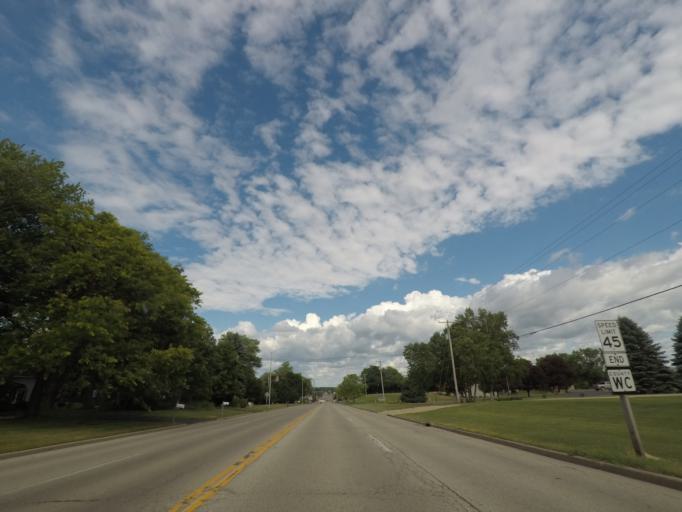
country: US
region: Wisconsin
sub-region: Rock County
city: Janesville
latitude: 42.6791
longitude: -89.0592
